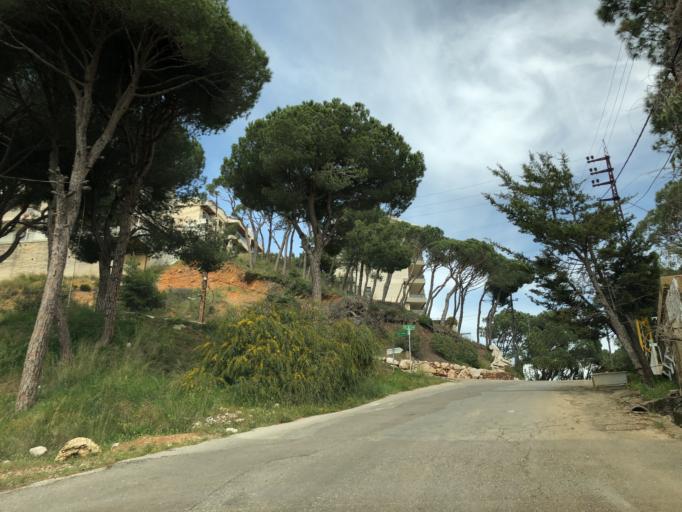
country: LB
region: Mont-Liban
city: Bhamdoun el Mhatta
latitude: 33.8871
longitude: 35.6562
